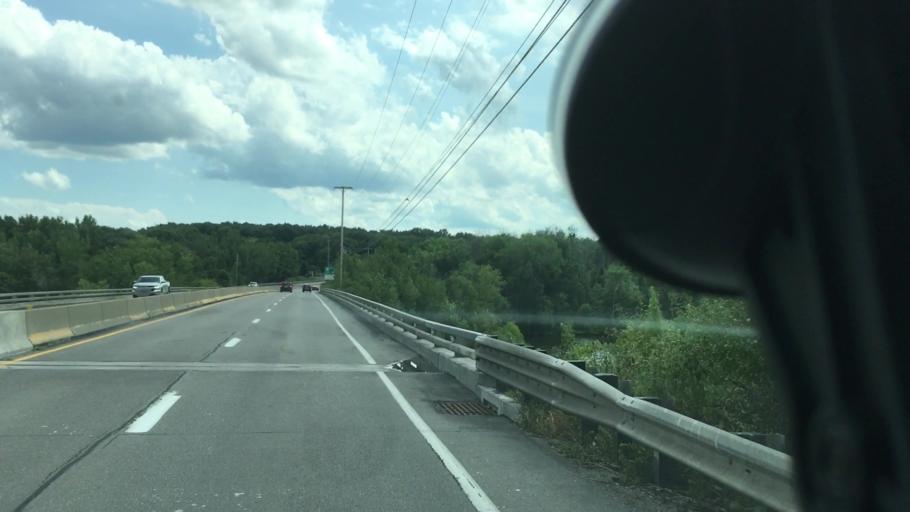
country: US
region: Pennsylvania
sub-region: Mercer County
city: Sharpsville
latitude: 41.2875
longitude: -80.4281
